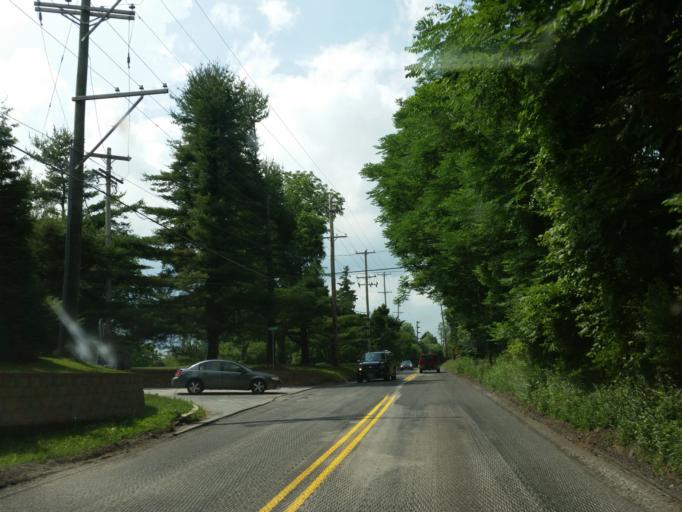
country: US
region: Pennsylvania
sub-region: Chester County
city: West Grove
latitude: 39.7851
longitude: -75.8790
